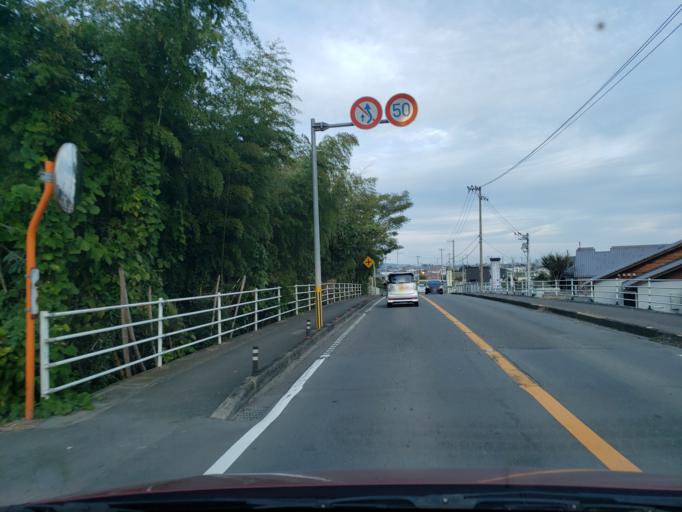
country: JP
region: Tokushima
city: Kamojimacho-jogejima
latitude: 34.0992
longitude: 134.3295
